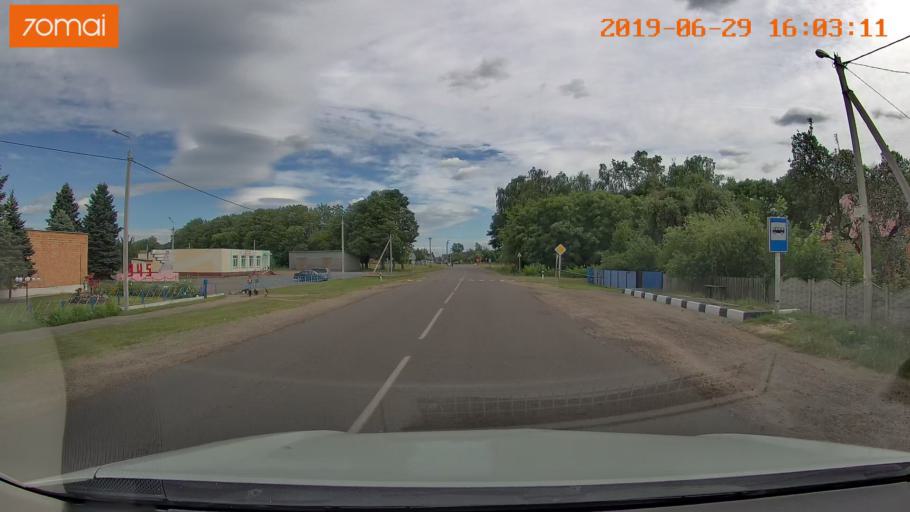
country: BY
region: Brest
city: Luninyets
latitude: 52.2304
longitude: 27.0183
